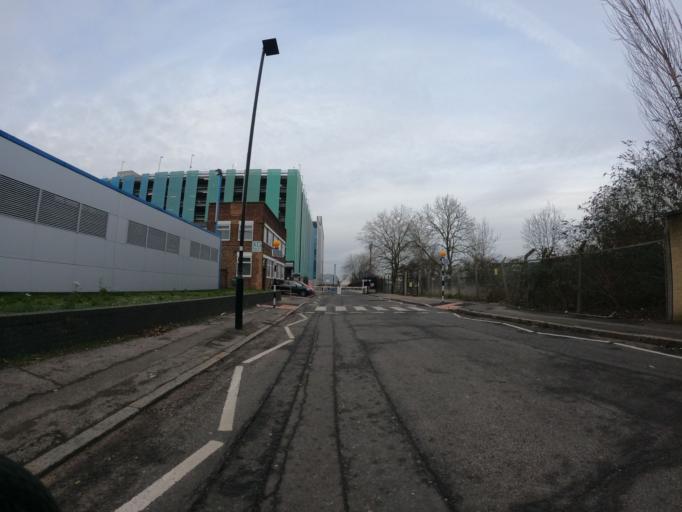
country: GB
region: England
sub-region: Greater London
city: Brentford
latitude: 51.4860
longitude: -0.3265
